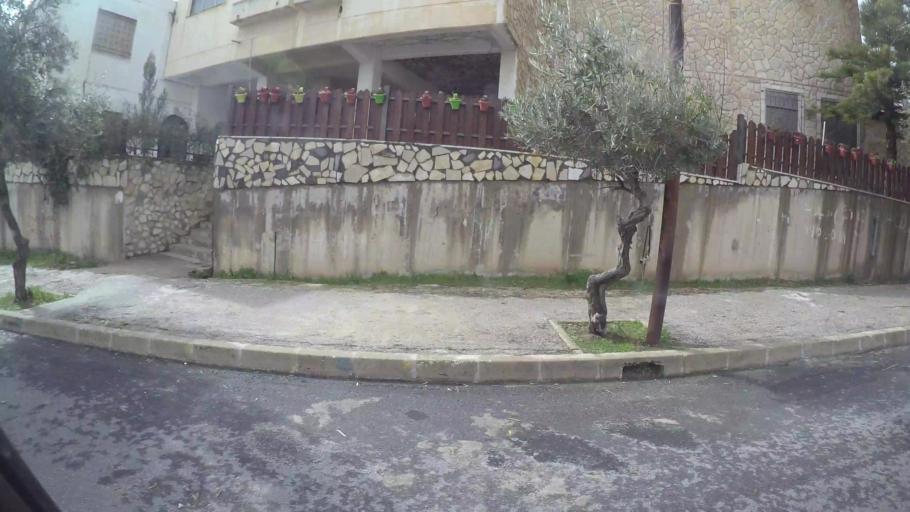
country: JO
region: Amman
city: Al Jubayhah
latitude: 32.0537
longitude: 35.8823
